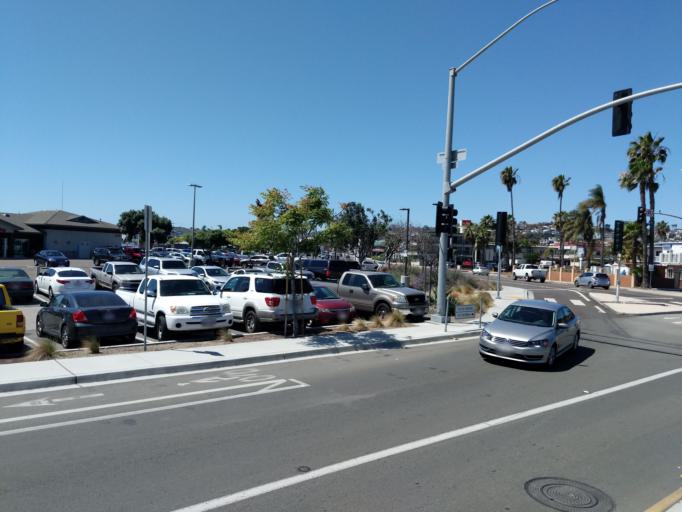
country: US
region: California
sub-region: San Diego County
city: Coronado
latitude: 32.7257
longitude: -117.2265
